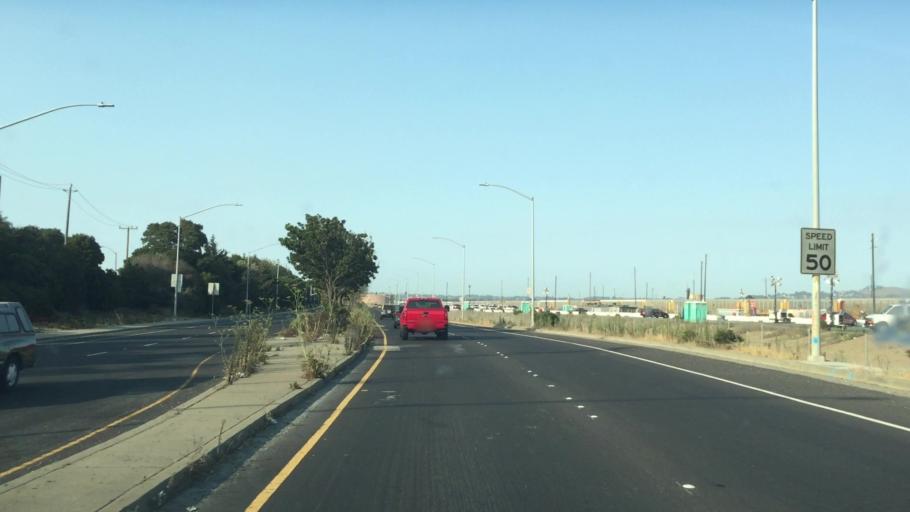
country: US
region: California
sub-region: Contra Costa County
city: North Richmond
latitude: 37.9312
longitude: -122.3836
